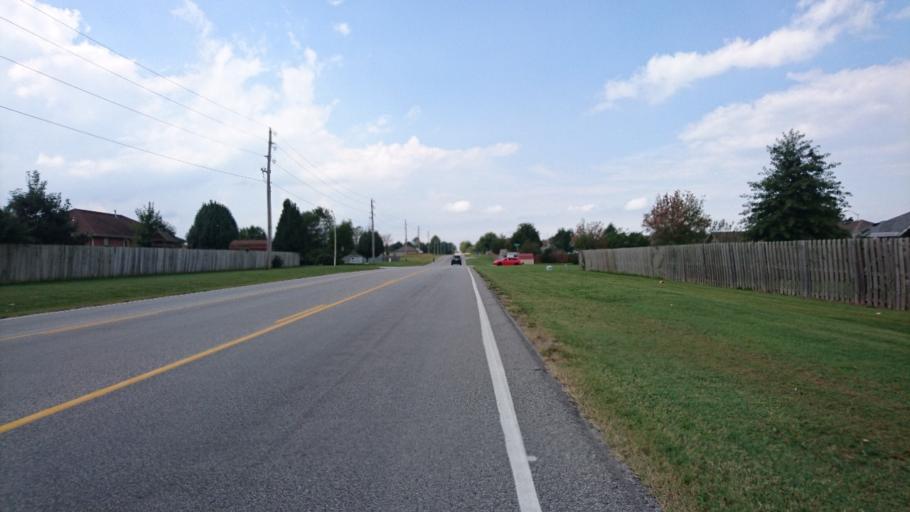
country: US
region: Missouri
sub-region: Greene County
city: Battlefield
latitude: 37.1981
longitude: -93.3925
